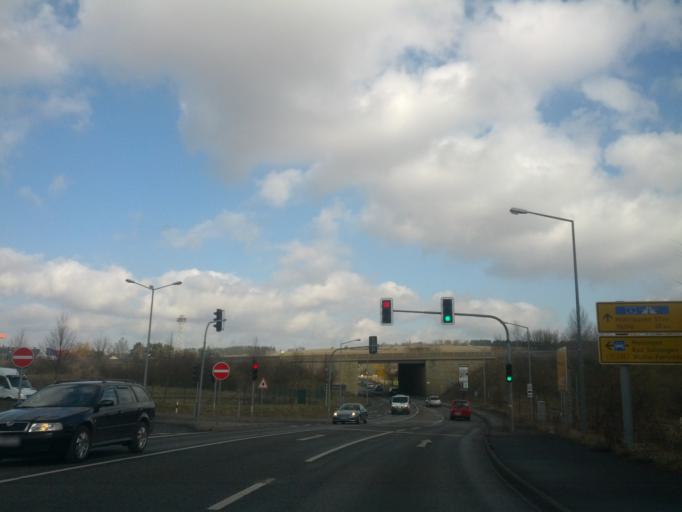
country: DE
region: Thuringia
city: Eisenach
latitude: 50.9957
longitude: 10.3169
